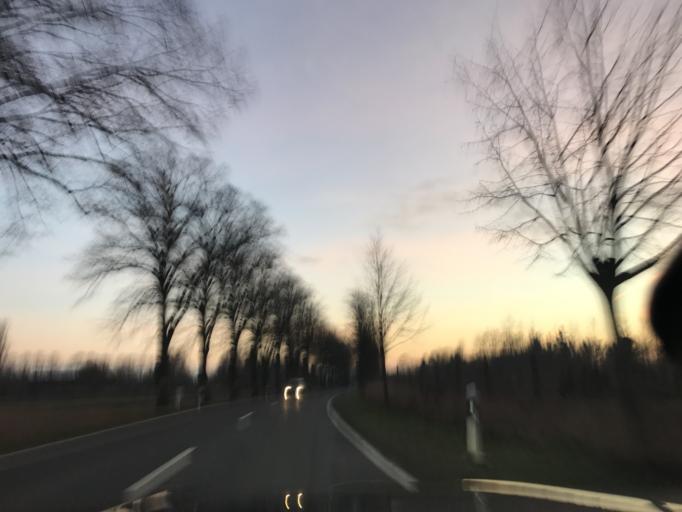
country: DE
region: Brandenburg
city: Ketzin
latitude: 52.4908
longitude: 12.8501
